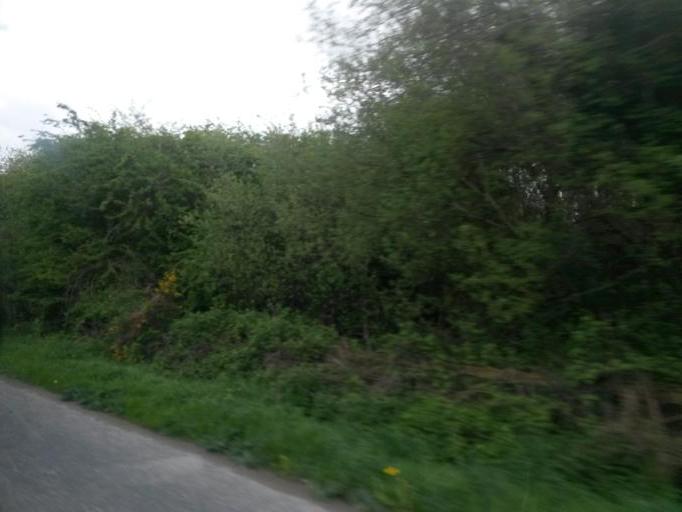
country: IE
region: Leinster
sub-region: Loch Garman
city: Enniscorthy
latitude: 52.4674
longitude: -6.5608
